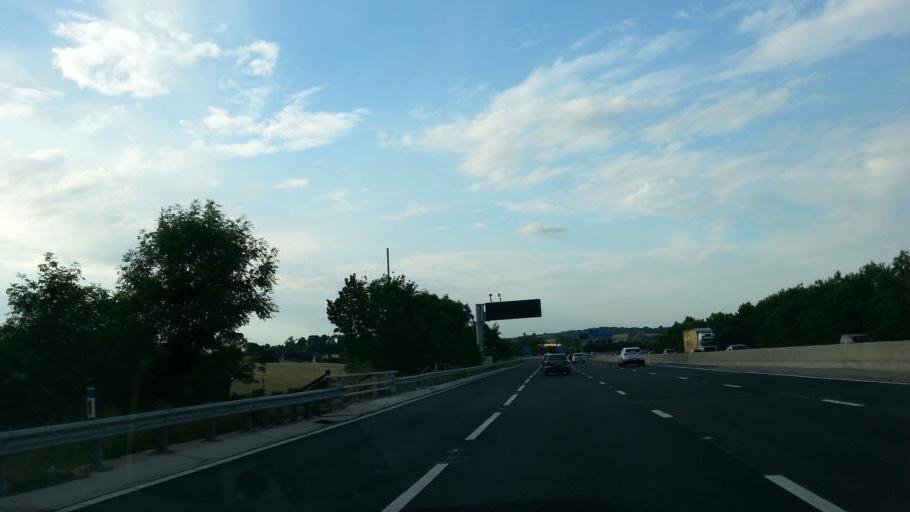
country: GB
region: England
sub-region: Worcestershire
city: Bromsgrove
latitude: 52.3331
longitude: -2.0844
